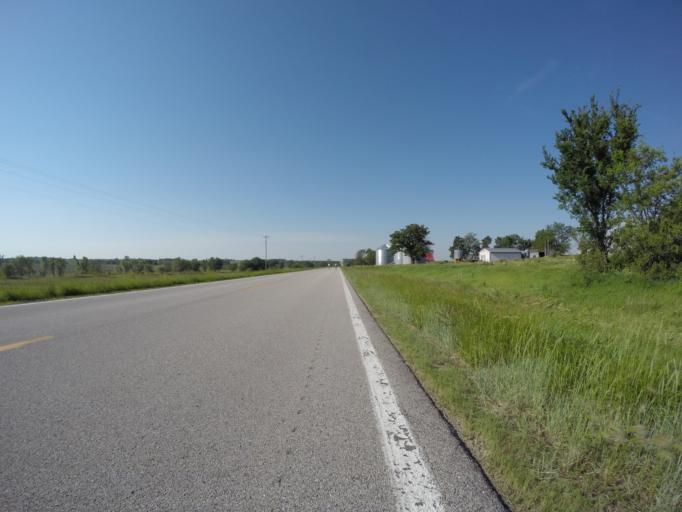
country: US
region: Nebraska
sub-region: Gage County
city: Wymore
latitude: 40.0496
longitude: -96.4828
